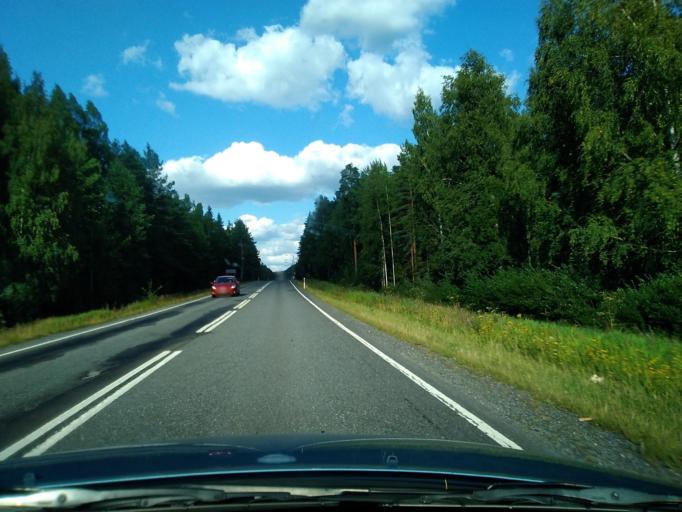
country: FI
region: Pirkanmaa
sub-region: Ylae-Pirkanmaa
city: Maenttae
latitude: 62.0174
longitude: 24.6809
